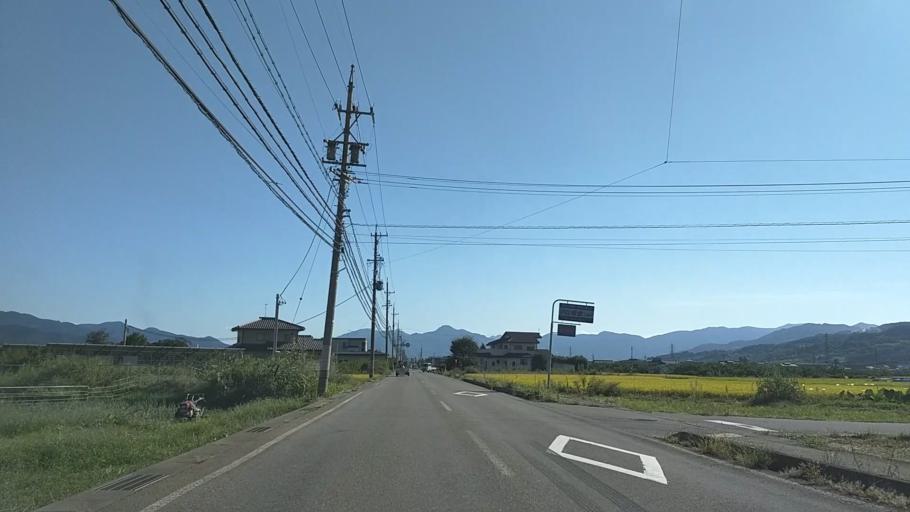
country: JP
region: Nagano
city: Nagano-shi
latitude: 36.6077
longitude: 138.1434
